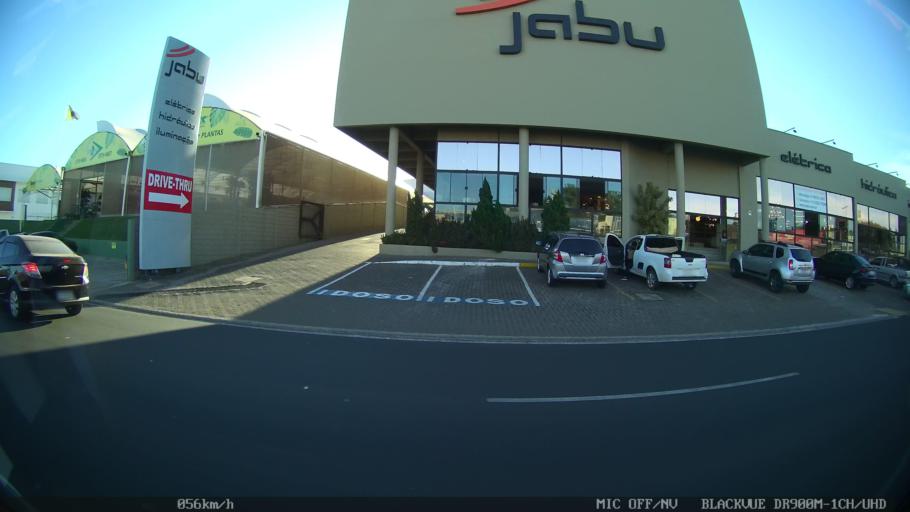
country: BR
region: Sao Paulo
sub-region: Araraquara
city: Araraquara
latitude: -21.7808
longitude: -48.1708
